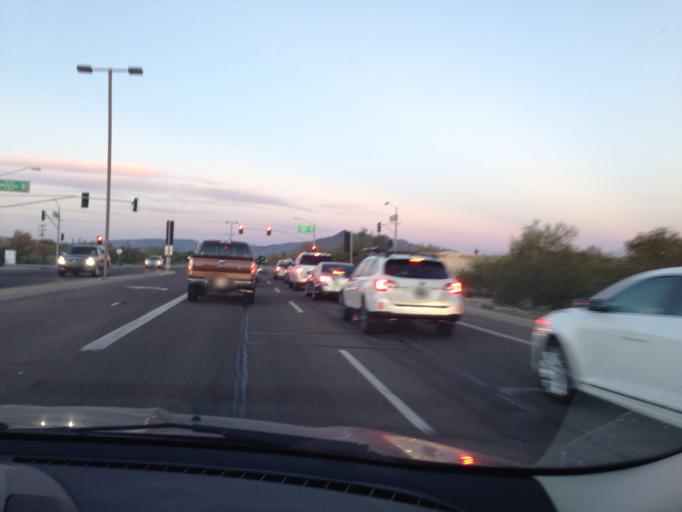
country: US
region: Arizona
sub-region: Maricopa County
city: Cave Creek
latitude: 33.7662
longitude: -111.9842
